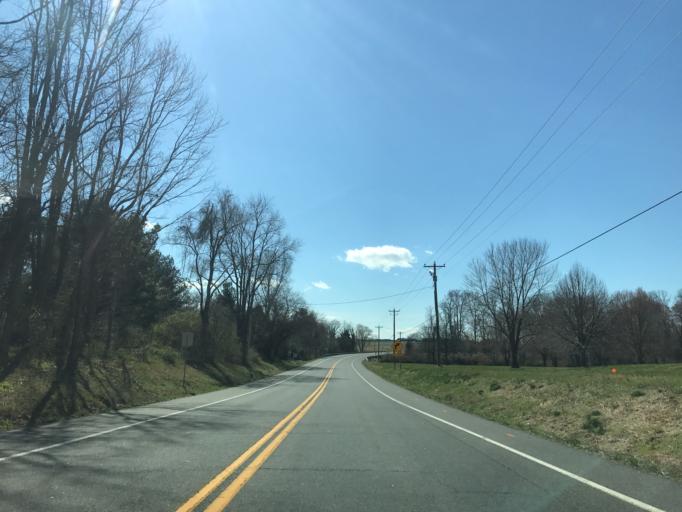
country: US
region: Maryland
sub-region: Kent County
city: Chestertown
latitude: 39.2122
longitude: -76.0965
